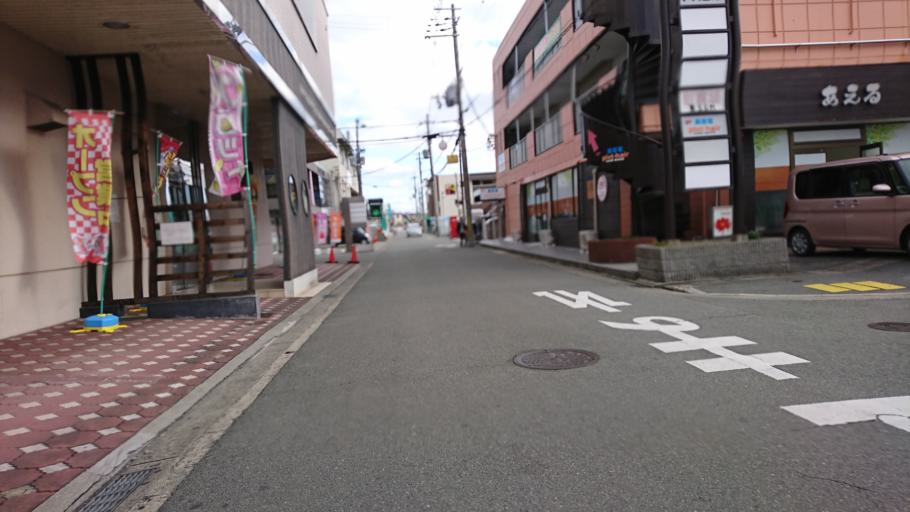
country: JP
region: Hyogo
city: Kakogawacho-honmachi
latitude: 34.7851
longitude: 134.8128
